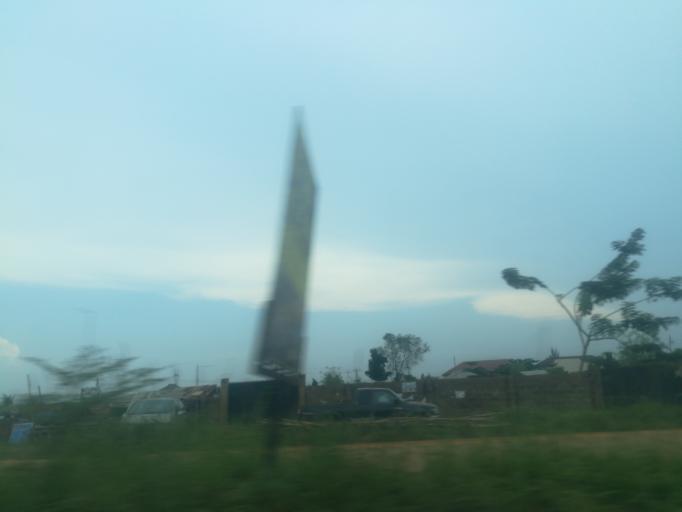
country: NG
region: Oyo
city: Ibadan
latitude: 7.3663
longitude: 3.8137
